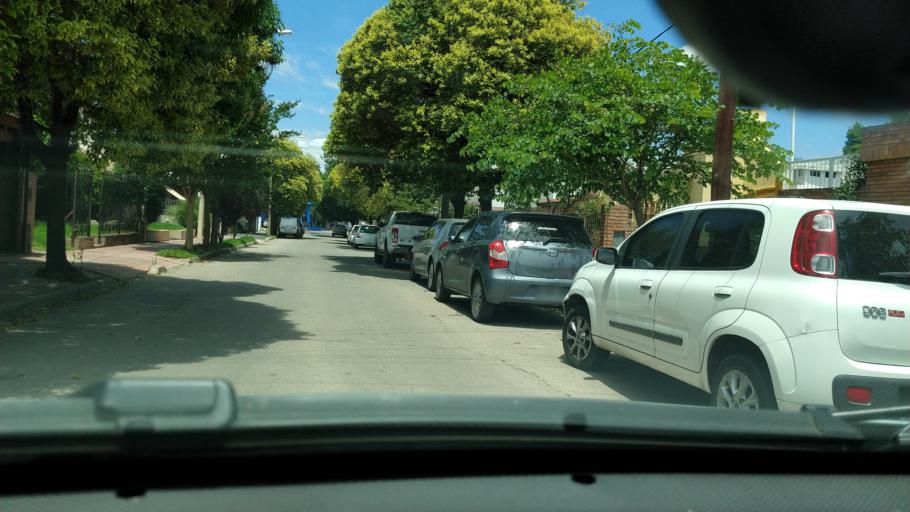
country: AR
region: Cordoba
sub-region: Departamento de Capital
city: Cordoba
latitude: -31.3607
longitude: -64.2302
